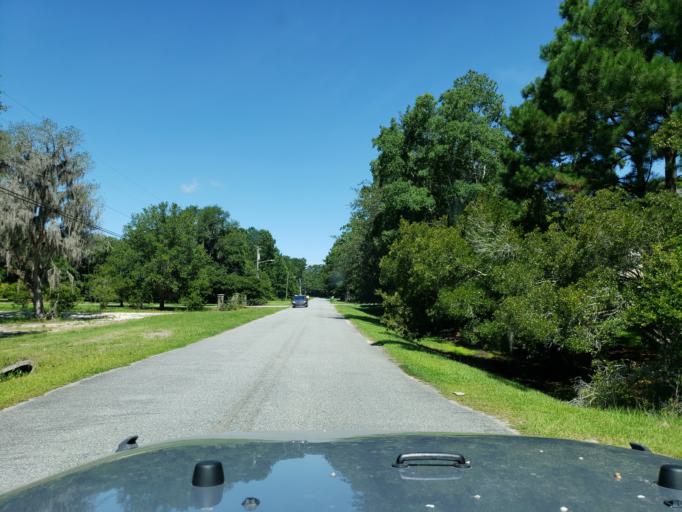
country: US
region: Georgia
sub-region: Chatham County
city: Georgetown
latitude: 31.9628
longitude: -81.2144
